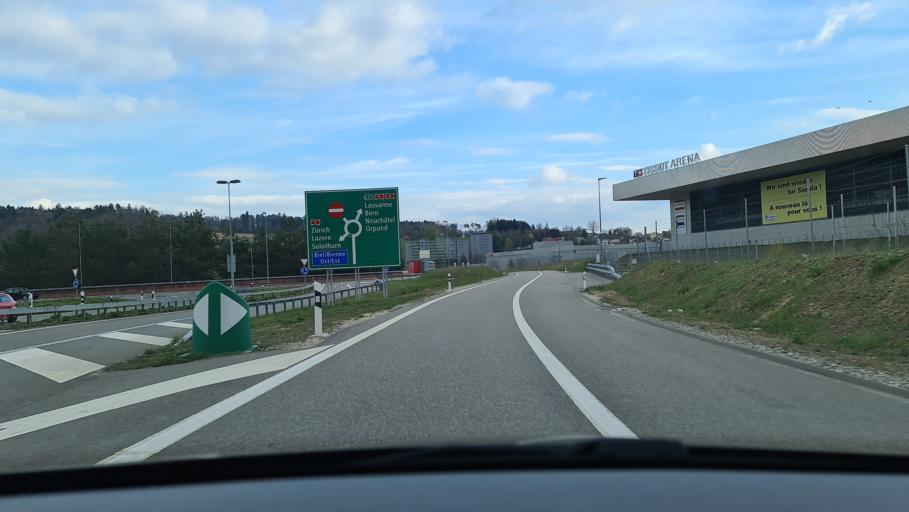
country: CH
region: Bern
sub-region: Biel/Bienne District
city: Orpund
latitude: 47.1582
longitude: 7.2834
